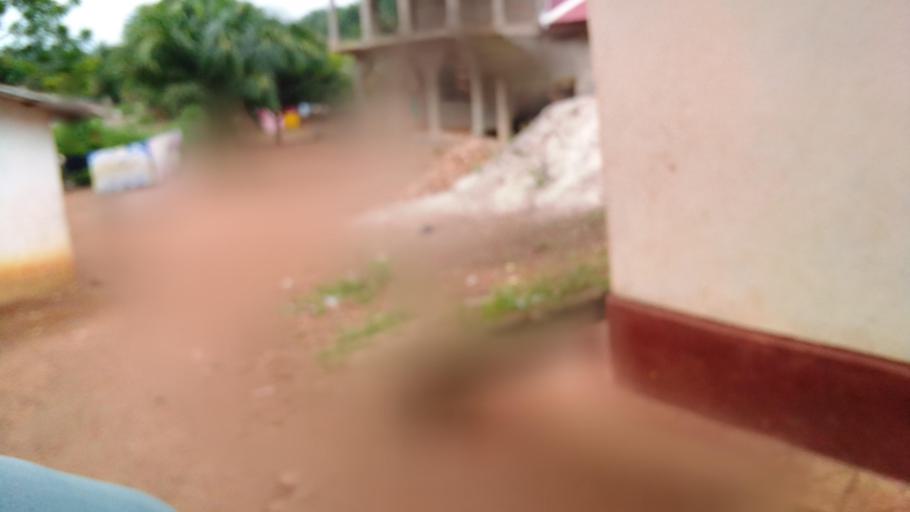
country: SL
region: Eastern Province
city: Kenema
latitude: 7.8549
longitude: -11.1890
